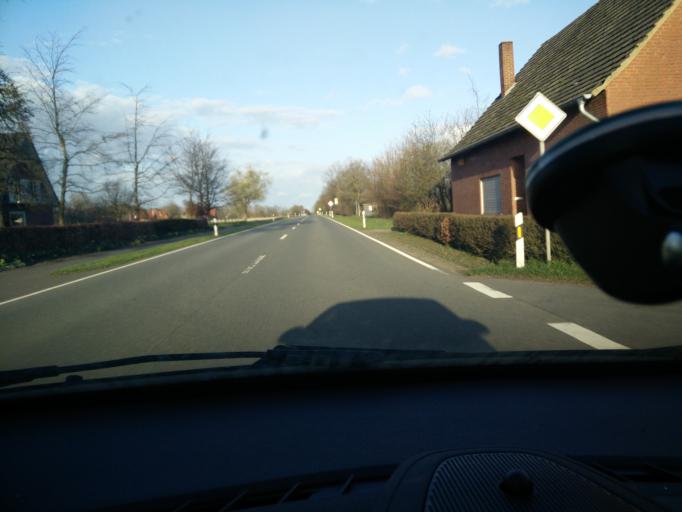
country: DE
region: North Rhine-Westphalia
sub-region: Regierungsbezirk Munster
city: Raesfeld
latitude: 51.7640
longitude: 6.8102
